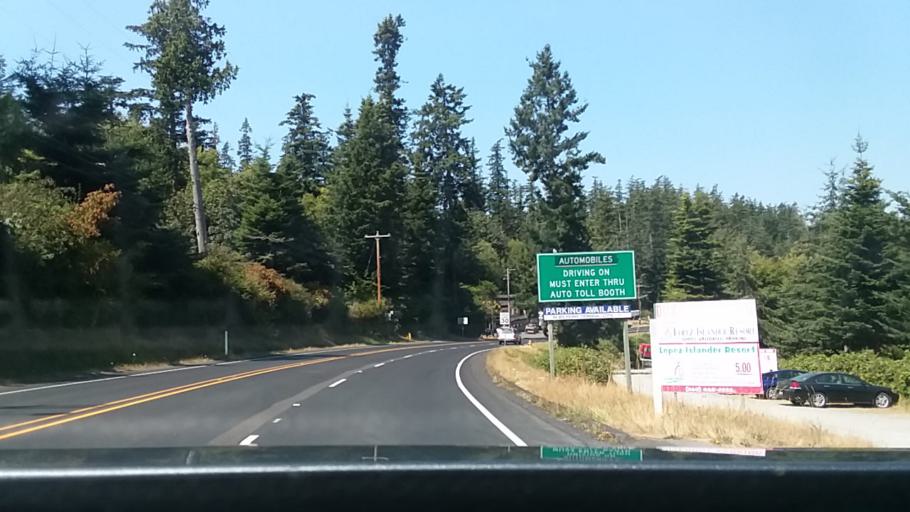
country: US
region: Washington
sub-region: Skagit County
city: Anacortes
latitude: 48.5000
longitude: -122.6771
